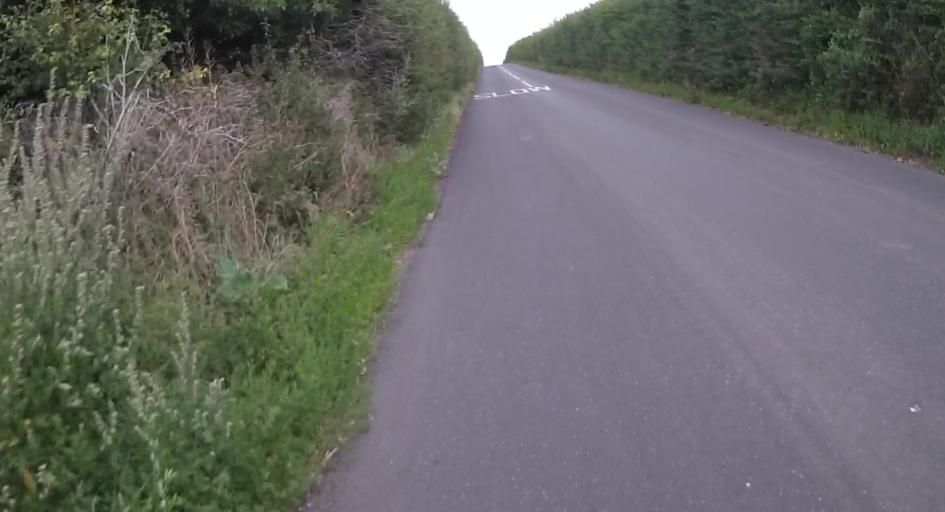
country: GB
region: England
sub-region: Hampshire
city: Kings Worthy
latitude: 51.1416
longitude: -1.3071
